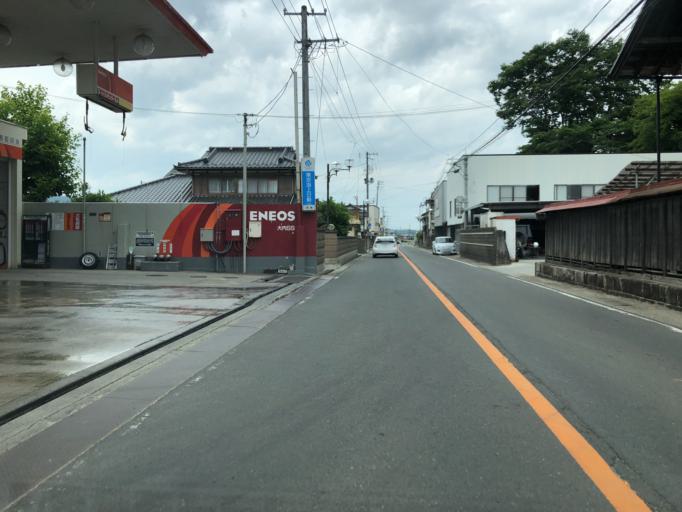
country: JP
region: Miyagi
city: Marumori
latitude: 37.8691
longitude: 140.8252
